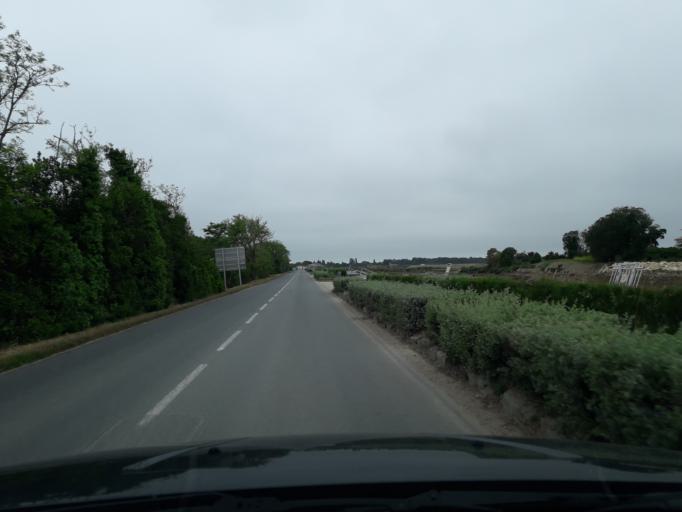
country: FR
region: Poitou-Charentes
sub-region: Departement de la Charente-Maritime
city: Boyard-Ville
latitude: 45.9635
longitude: -1.2449
